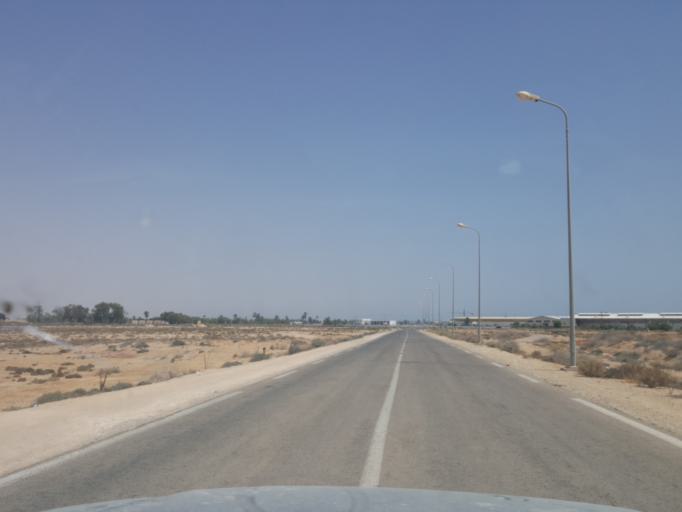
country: TN
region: Qabis
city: Gabes
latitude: 33.9780
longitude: 10.0033
